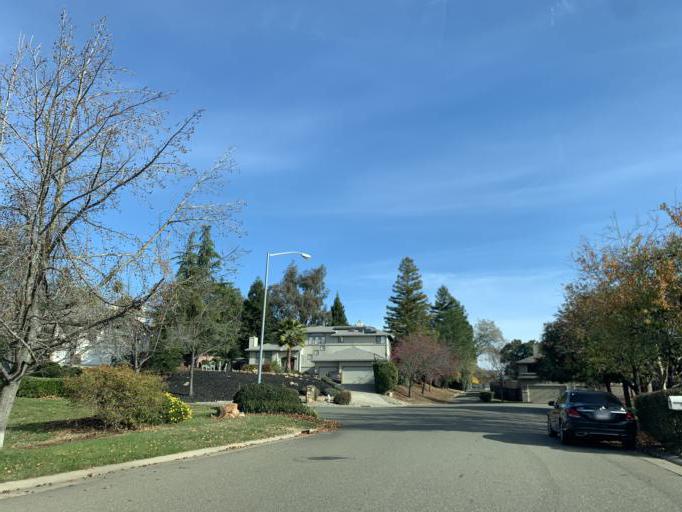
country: US
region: California
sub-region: El Dorado County
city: El Dorado Hills
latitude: 38.6533
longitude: -121.0763
